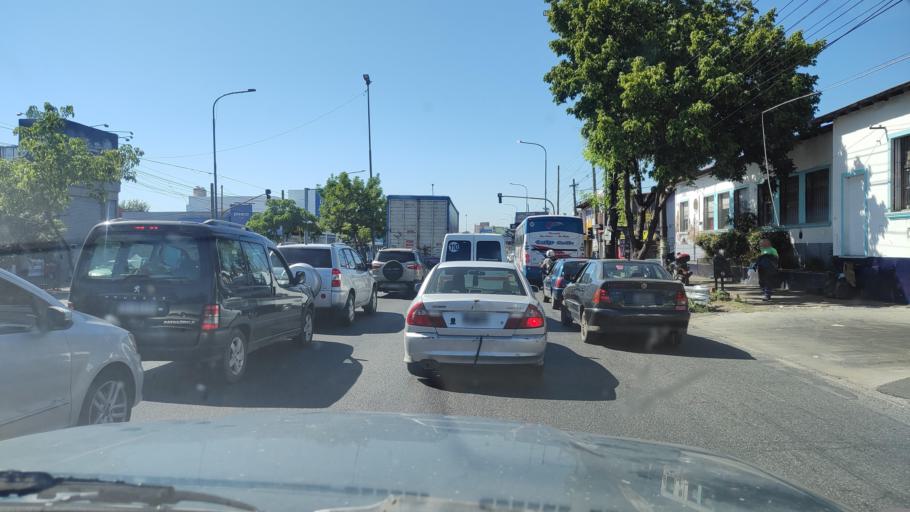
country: AR
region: Buenos Aires
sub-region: Partido de Moron
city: Moron
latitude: -34.6375
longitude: -58.6270
